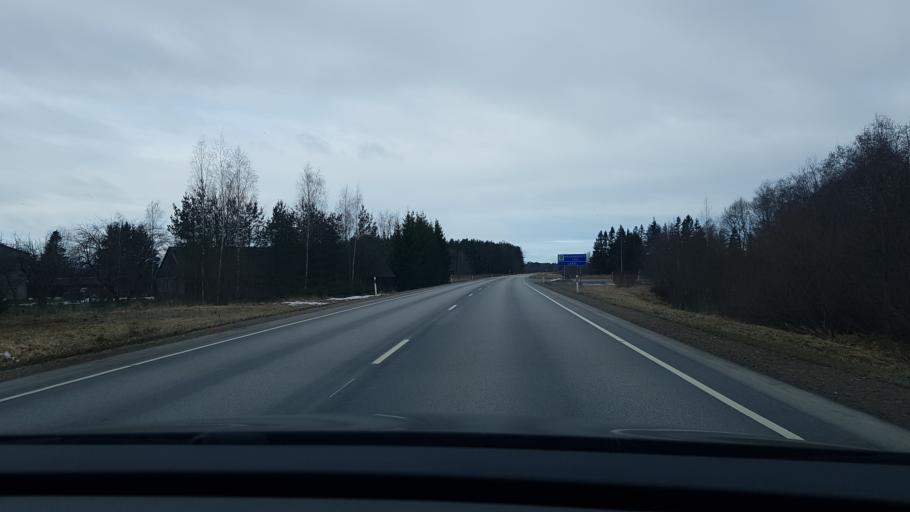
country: EE
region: Paernumaa
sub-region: Paikuse vald
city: Paikuse
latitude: 58.2678
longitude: 24.6440
